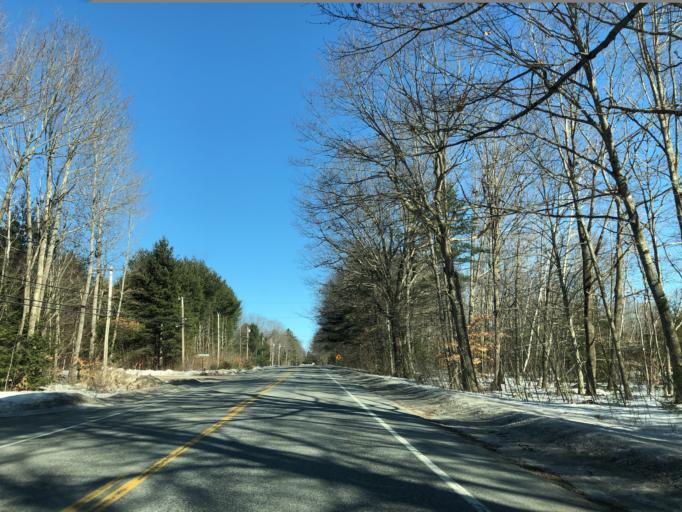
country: US
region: Maine
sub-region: Cumberland County
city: South Windham
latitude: 43.7644
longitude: -70.4223
